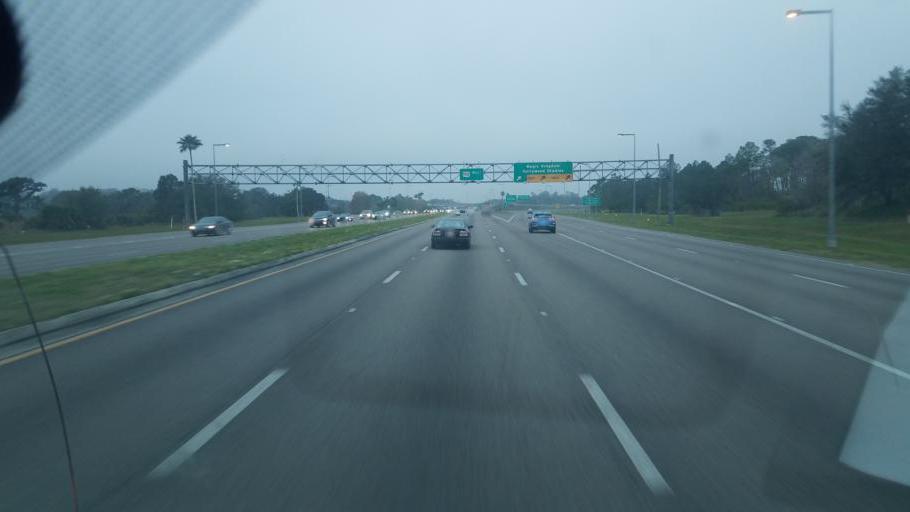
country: US
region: Florida
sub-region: Osceola County
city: Celebration
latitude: 28.3330
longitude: -81.5582
